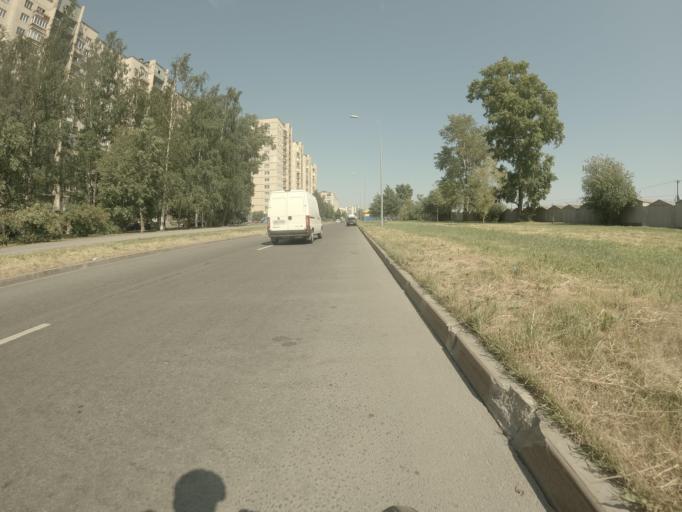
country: RU
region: St.-Petersburg
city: Krasnogvargeisky
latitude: 59.9371
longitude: 30.5008
